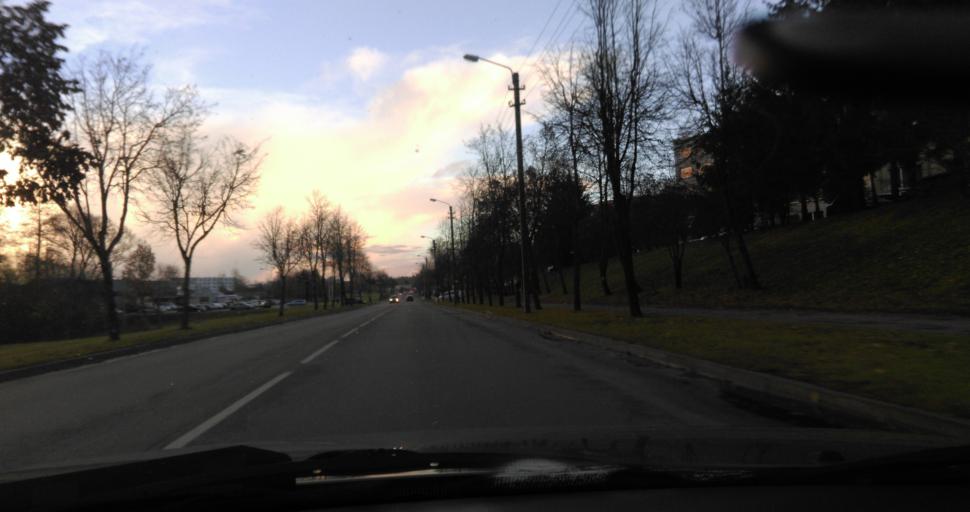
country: LT
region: Utenos apskritis
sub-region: Utena
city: Utena
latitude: 55.5113
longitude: 25.6018
